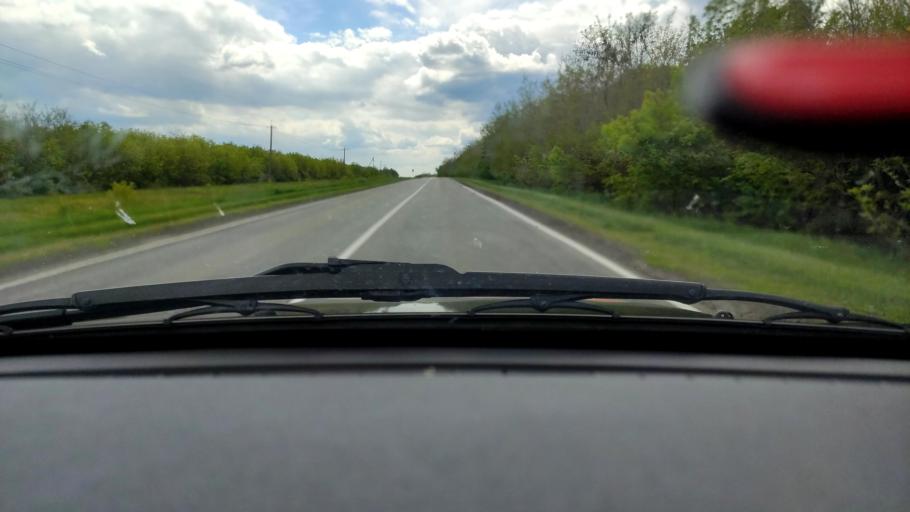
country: RU
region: Voronezj
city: Uryv-Pokrovka
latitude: 51.1000
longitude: 39.0155
